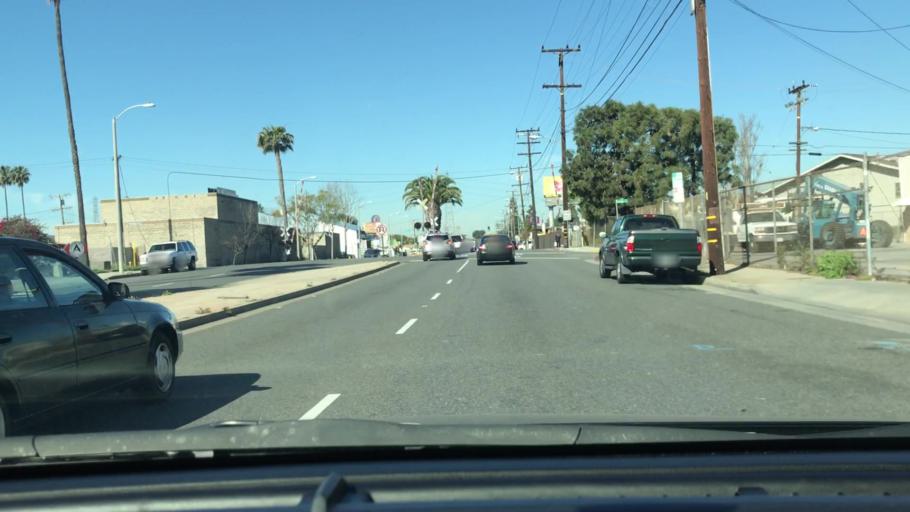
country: US
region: California
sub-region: Los Angeles County
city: Lawndale
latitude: 33.8875
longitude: -118.3589
